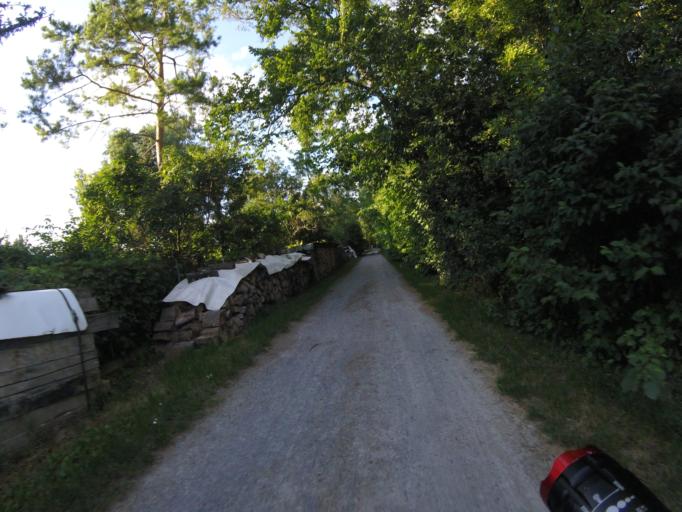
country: AT
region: Lower Austria
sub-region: Politischer Bezirk Modling
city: Munchendorf
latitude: 48.0208
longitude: 16.3719
